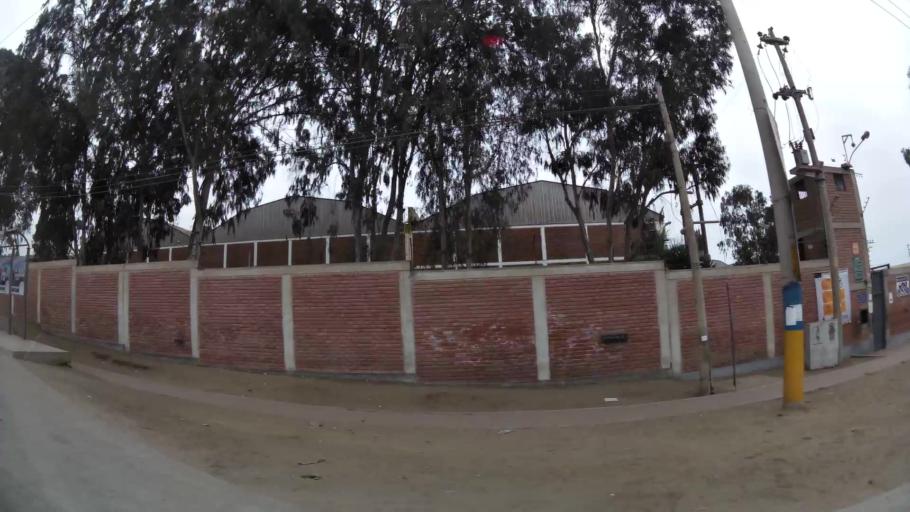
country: PE
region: Lima
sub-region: Lima
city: Surco
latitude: -12.2101
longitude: -76.9601
